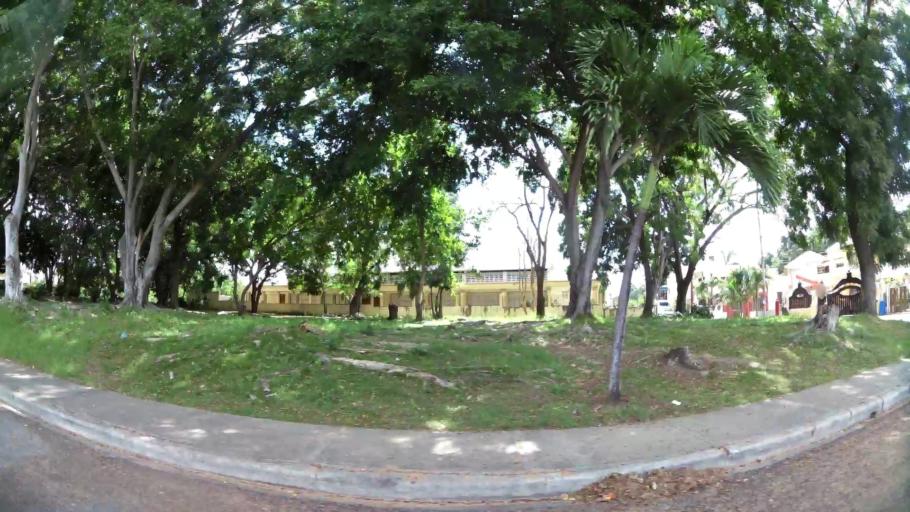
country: DO
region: Santiago
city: Santiago de los Caballeros
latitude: 19.4713
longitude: -70.6959
